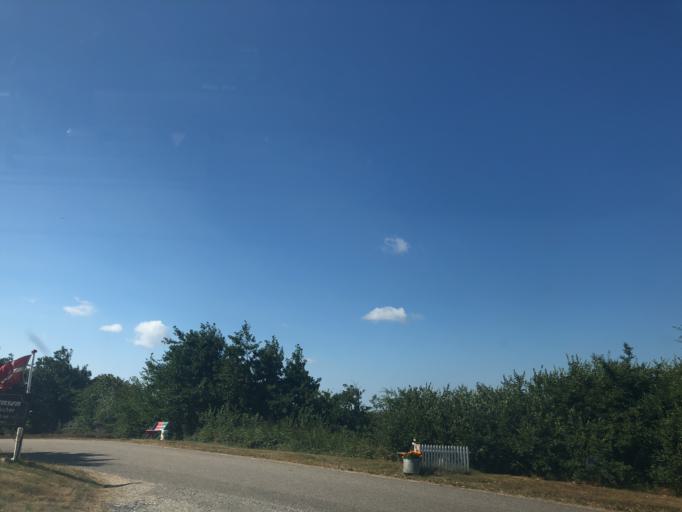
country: DK
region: North Denmark
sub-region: Morso Kommune
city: Nykobing Mors
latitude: 56.8046
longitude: 8.9982
